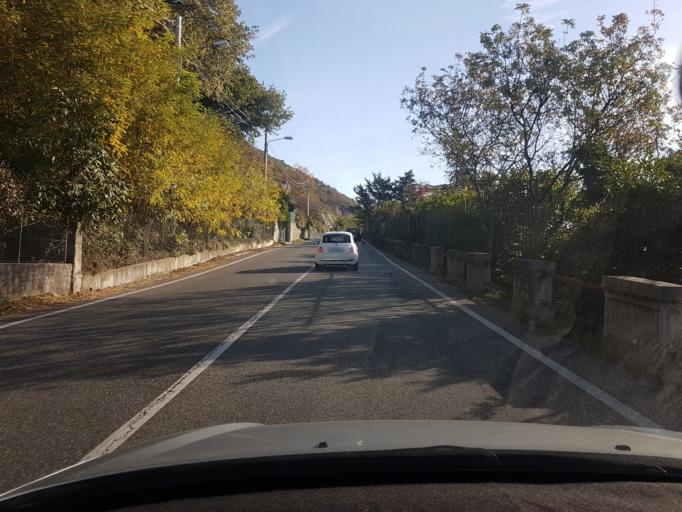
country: IT
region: Friuli Venezia Giulia
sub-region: Provincia di Trieste
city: Trieste
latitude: 45.6498
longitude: 13.8211
